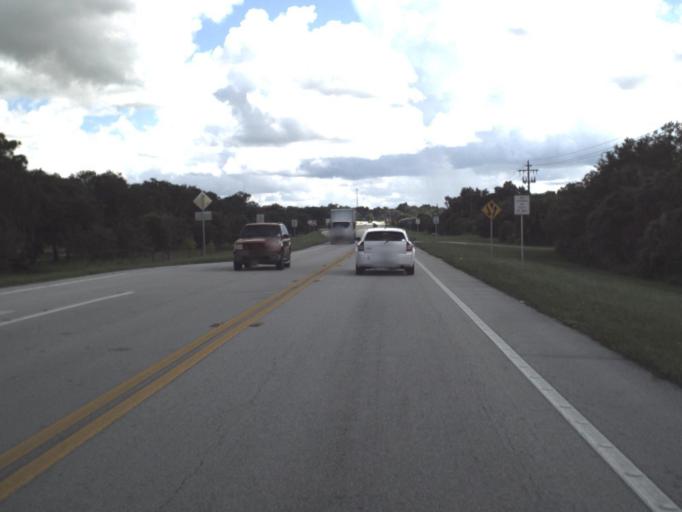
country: US
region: Florida
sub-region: DeSoto County
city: Arcadia
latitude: 27.2228
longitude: -81.8817
